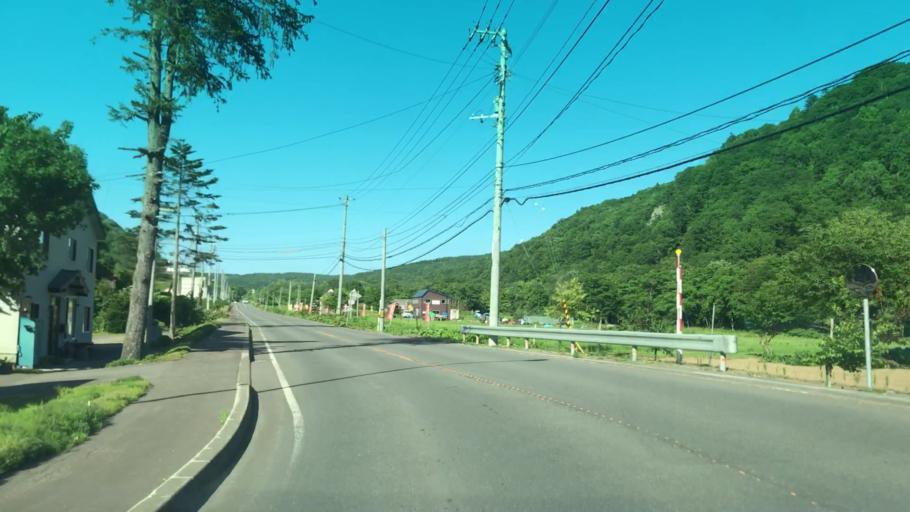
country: JP
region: Hokkaido
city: Yoichi
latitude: 43.0528
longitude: 140.8593
